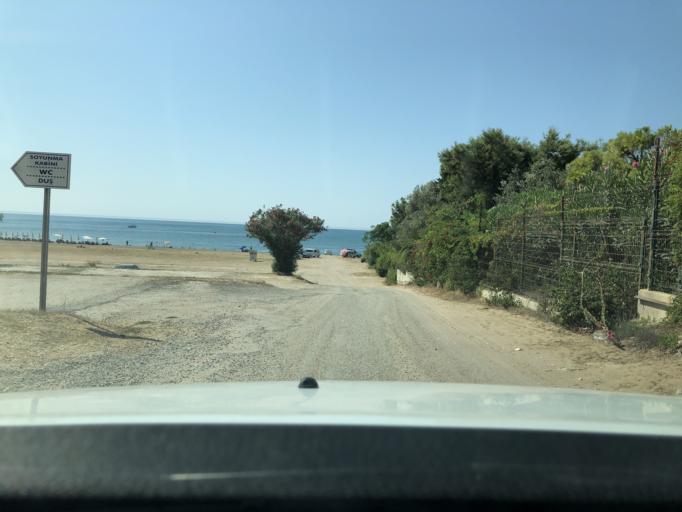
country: TR
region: Antalya
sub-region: Manavgat
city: Side
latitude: 36.7573
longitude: 31.4230
